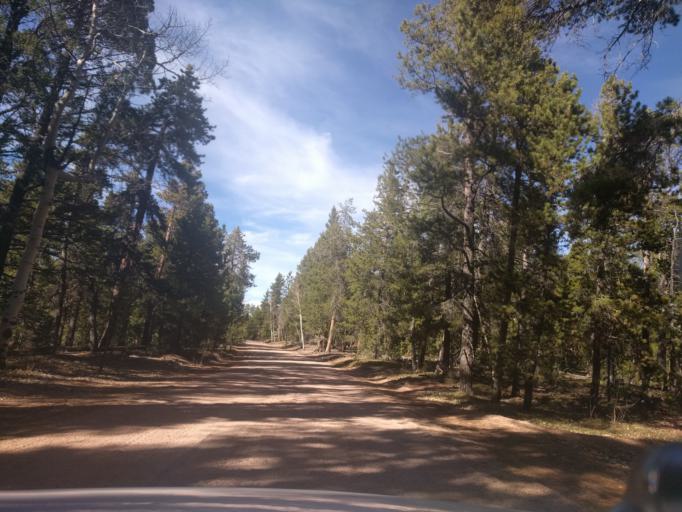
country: US
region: Colorado
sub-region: Douglas County
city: Perry Park
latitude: 39.2130
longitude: -105.0573
